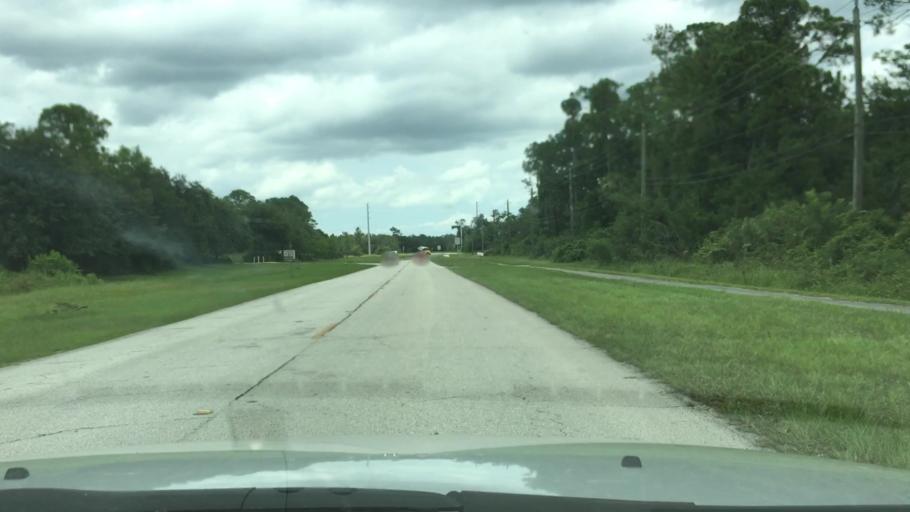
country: US
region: Florida
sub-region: Volusia County
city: Holly Hill
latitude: 29.2303
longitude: -81.0702
